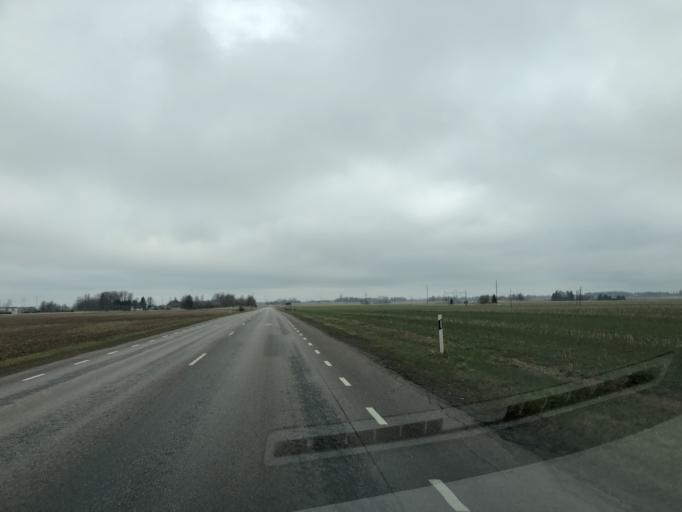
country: EE
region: Laeaene-Virumaa
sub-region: Vaeike-Maarja vald
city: Vaike-Maarja
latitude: 59.2033
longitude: 26.2689
